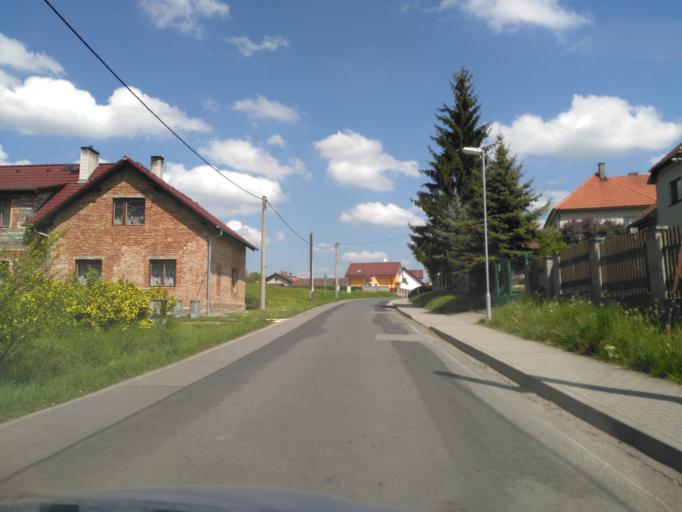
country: CZ
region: Central Bohemia
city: Lochovice
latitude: 49.8446
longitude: 13.9755
